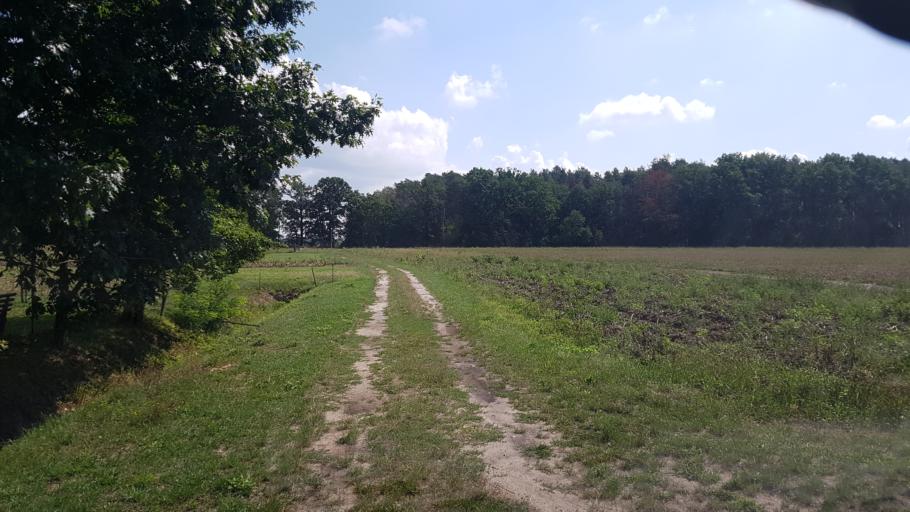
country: DE
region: Brandenburg
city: Sonnewalde
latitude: 51.6750
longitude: 13.6830
